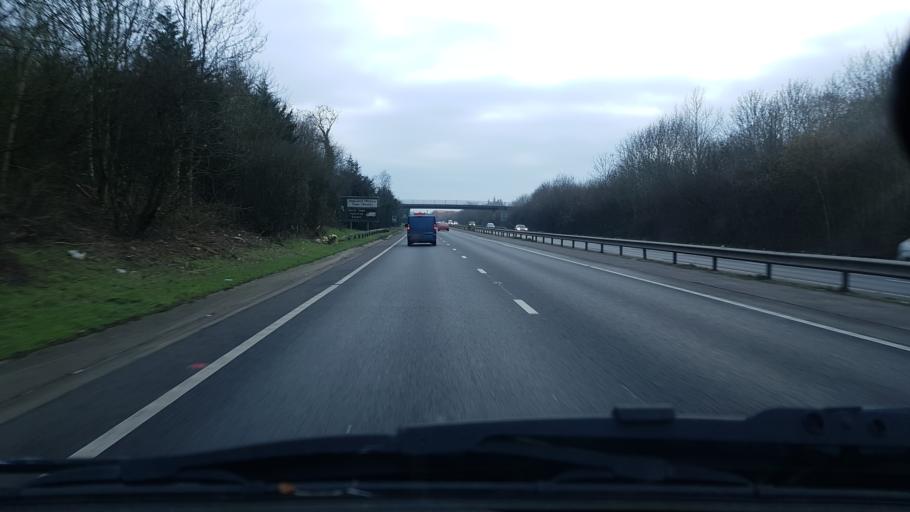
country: GB
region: England
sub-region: Surrey
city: Seale
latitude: 51.2498
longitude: -0.7312
